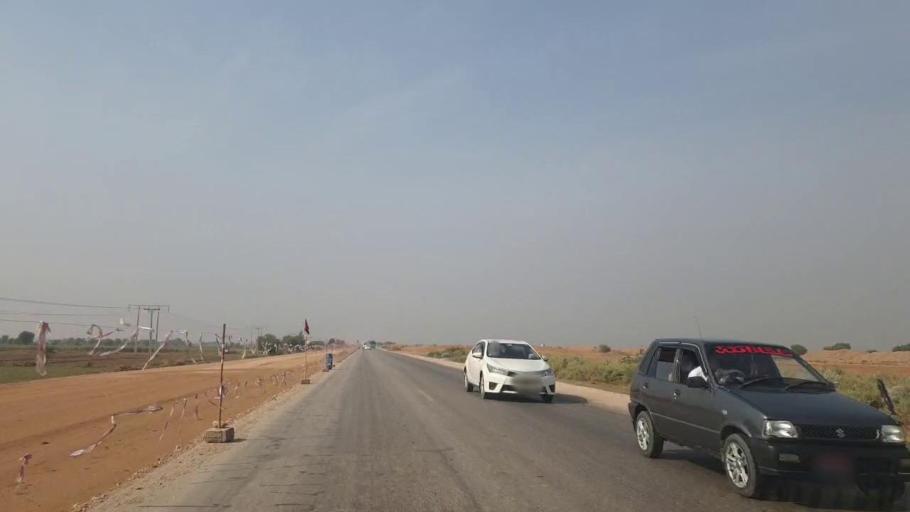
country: PK
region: Sindh
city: Sann
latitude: 26.1270
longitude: 68.0530
